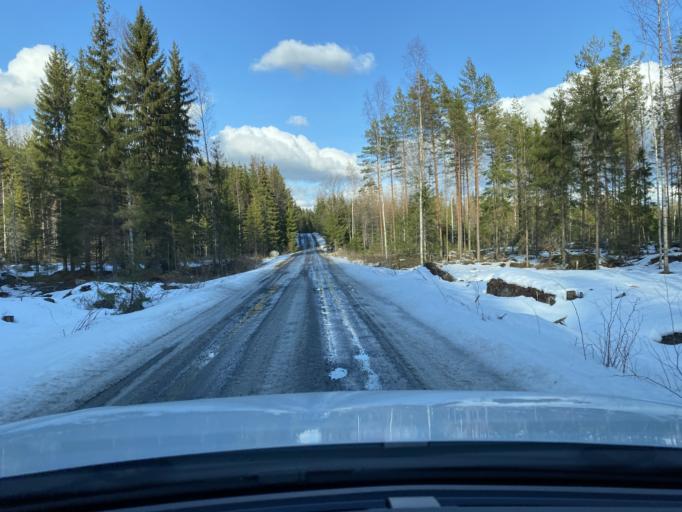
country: FI
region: Pirkanmaa
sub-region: Lounais-Pirkanmaa
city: Mouhijaervi
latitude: 61.4540
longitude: 22.9277
